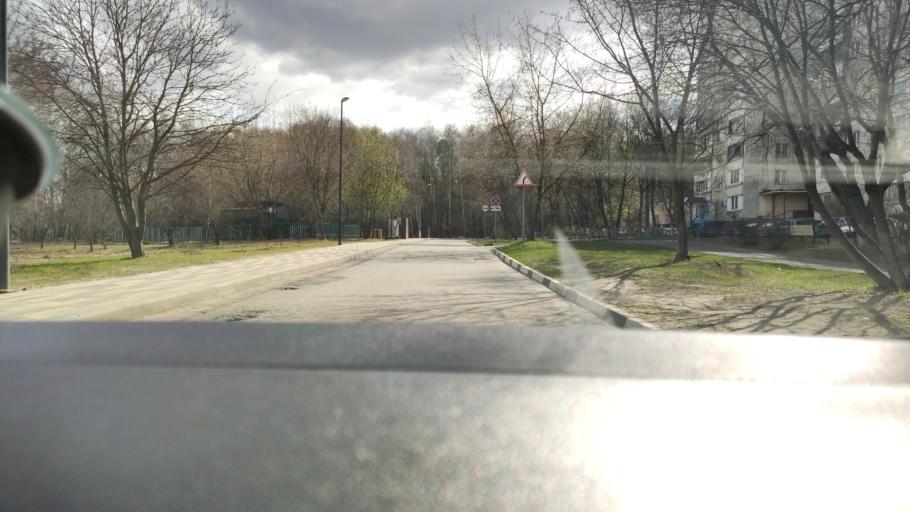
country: RU
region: Moskovskaya
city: Balashikha
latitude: 55.8209
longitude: 37.9575
